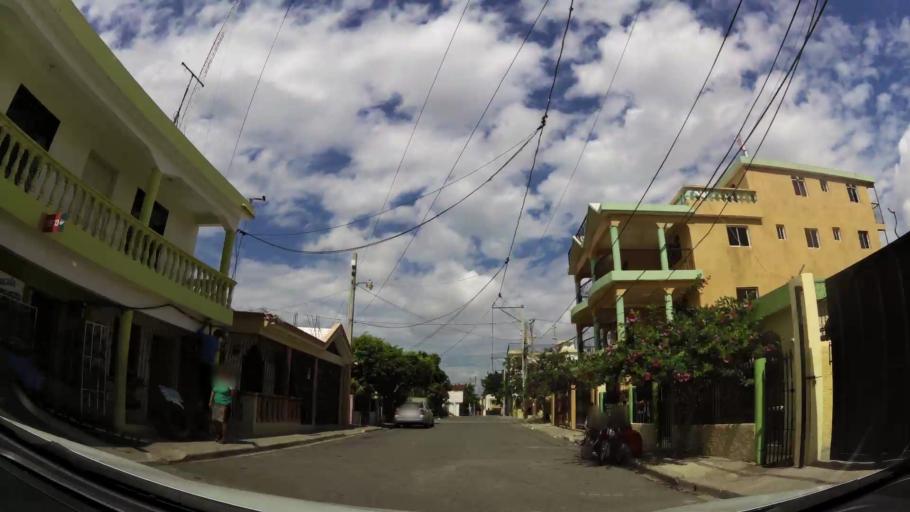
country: DO
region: Santiago
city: Santiago de los Caballeros
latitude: 19.4705
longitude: -70.6981
